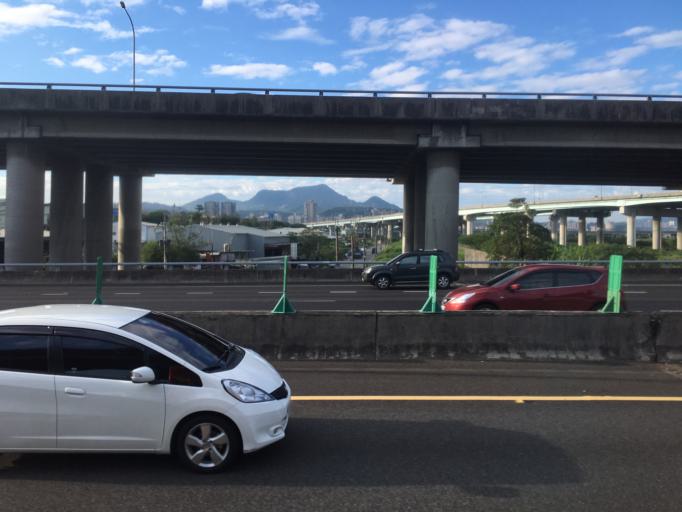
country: TW
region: Taipei
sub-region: Taipei
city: Banqiao
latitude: 25.0725
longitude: 121.4517
